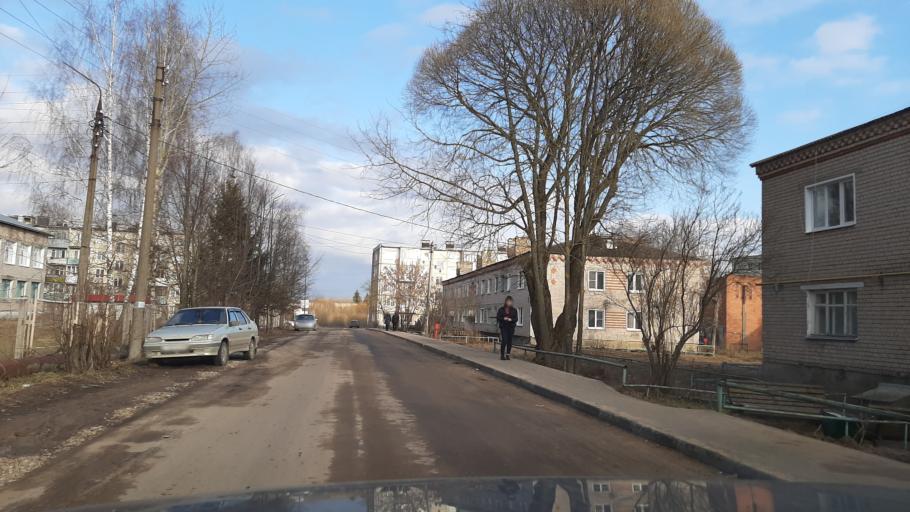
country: RU
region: Ivanovo
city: Novo-Talitsy
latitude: 56.9233
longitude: 40.7358
